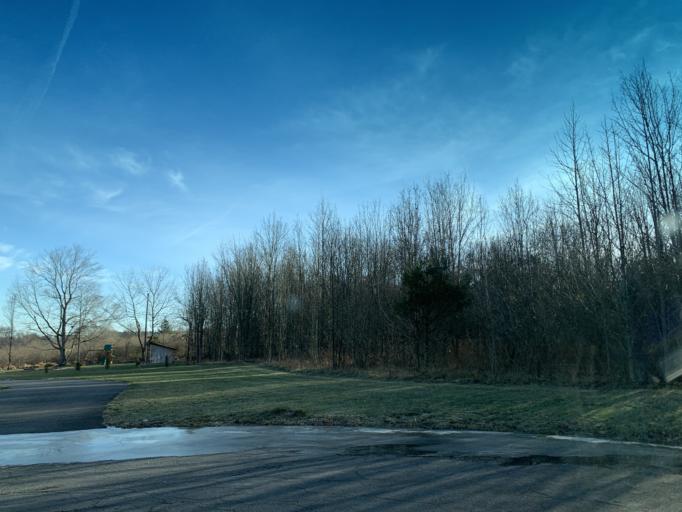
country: US
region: Maryland
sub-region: Harford County
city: Aberdeen
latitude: 39.5741
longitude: -76.1660
